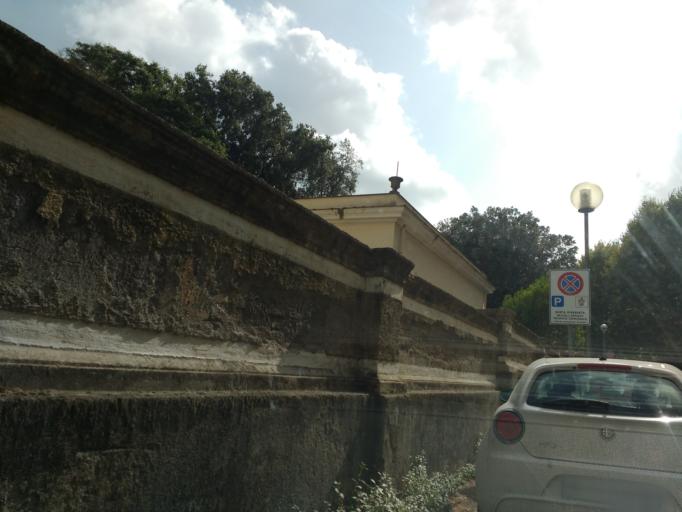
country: IT
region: Latium
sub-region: Citta metropolitana di Roma Capitale
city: Anzio
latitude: 41.4506
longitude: 12.6308
